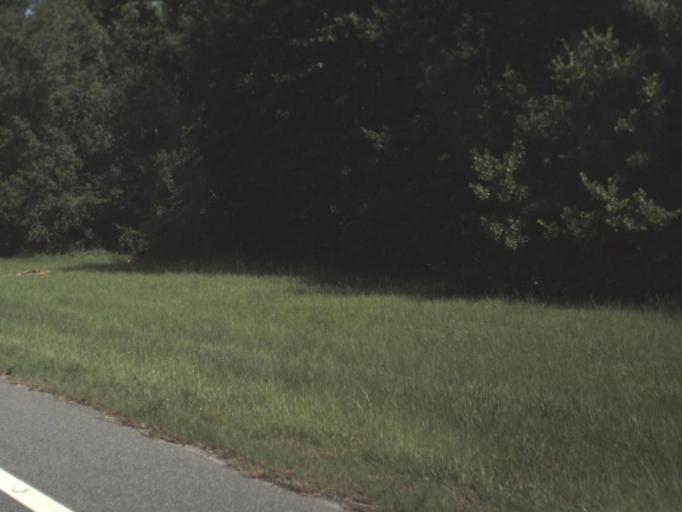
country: US
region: Florida
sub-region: Putnam County
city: Palatka
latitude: 29.6775
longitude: -81.7188
